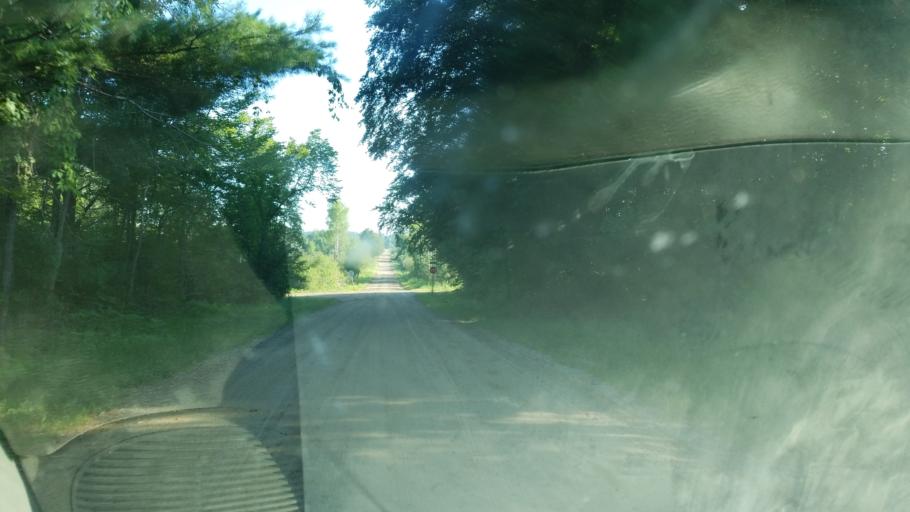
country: US
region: Michigan
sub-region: Mecosta County
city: Canadian Lakes
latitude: 43.5687
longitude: -85.4230
